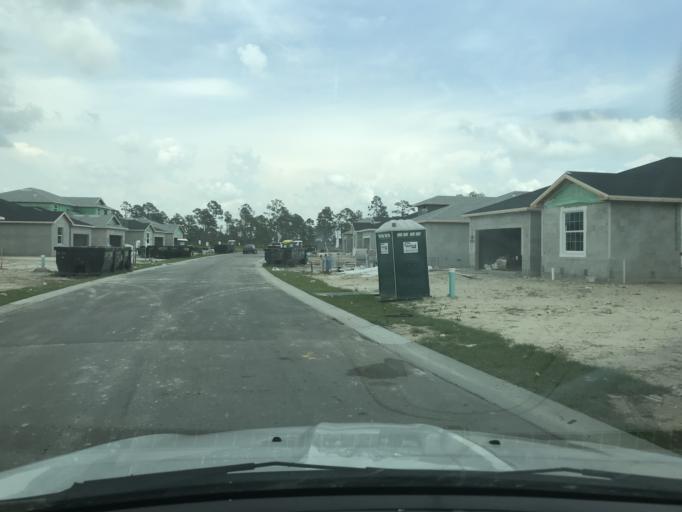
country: US
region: Florida
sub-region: Lee County
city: Olga
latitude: 26.7886
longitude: -81.7335
